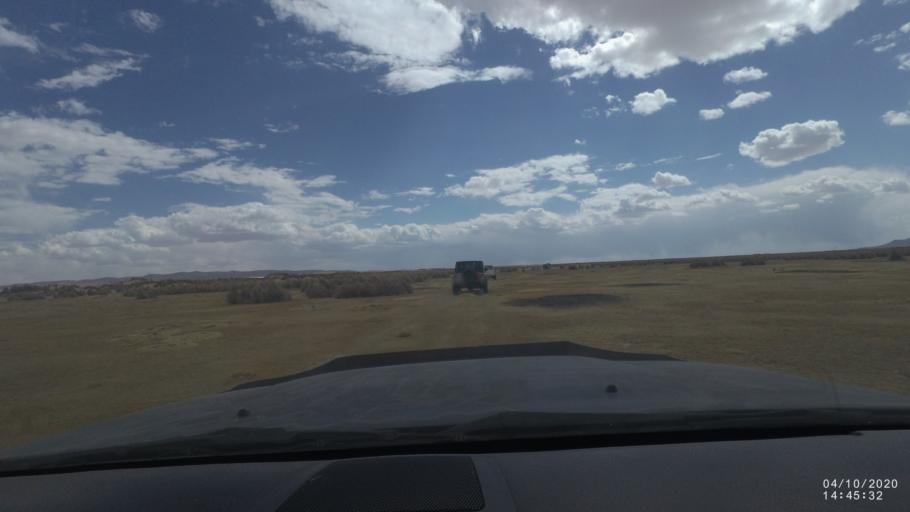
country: BO
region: Oruro
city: Poopo
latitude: -18.6864
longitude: -67.4989
